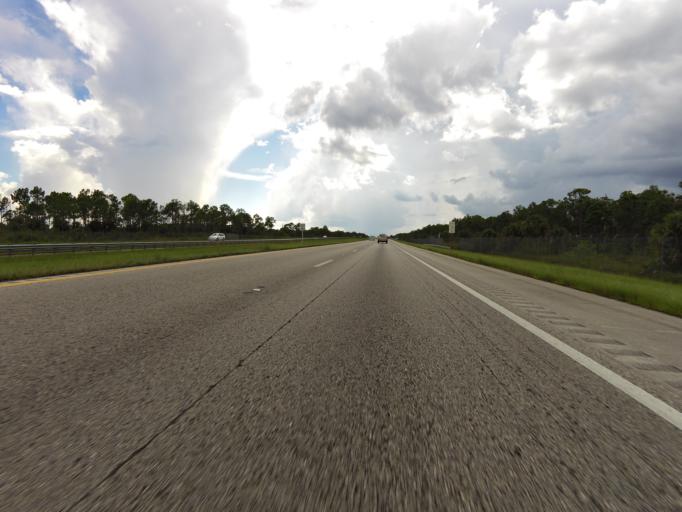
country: US
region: Florida
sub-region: Collier County
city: Orangetree
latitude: 26.1548
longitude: -81.3577
